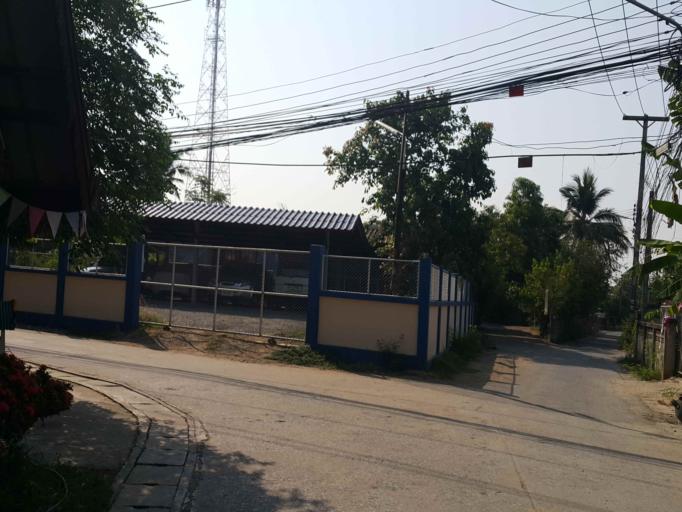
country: TH
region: Chiang Mai
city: San Kamphaeng
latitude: 18.7646
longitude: 99.0762
